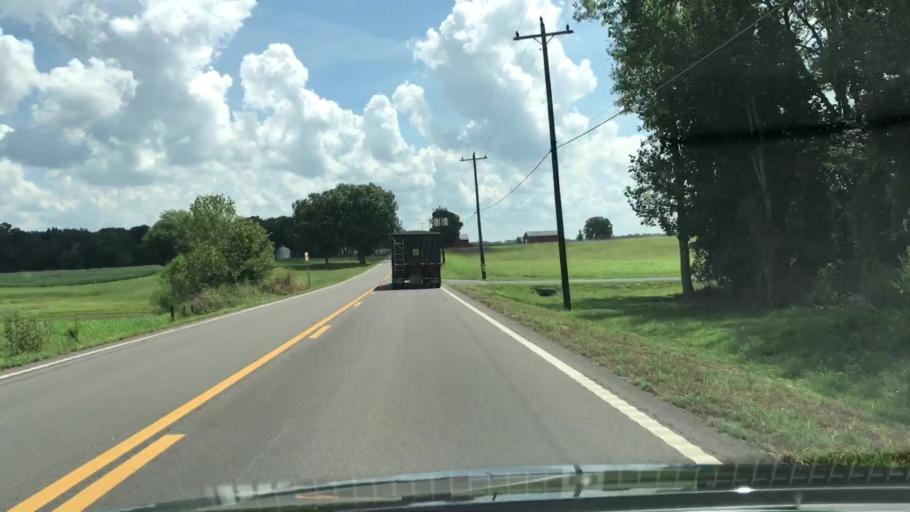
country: US
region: Tennessee
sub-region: Robertson County
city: Springfield
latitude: 36.6140
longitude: -86.9375
